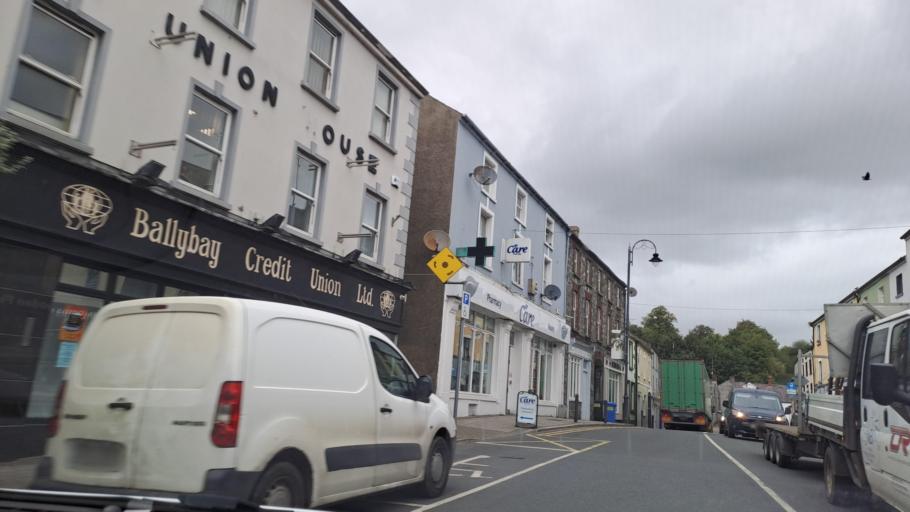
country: IE
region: Ulster
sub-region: County Monaghan
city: Monaghan
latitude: 54.1289
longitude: -6.9030
